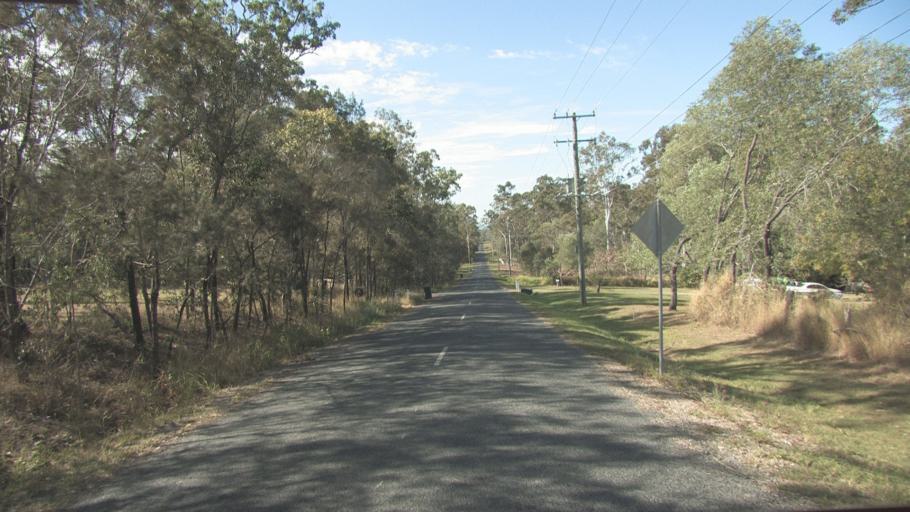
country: AU
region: Queensland
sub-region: Logan
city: North Maclean
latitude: -27.7652
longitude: 152.9705
